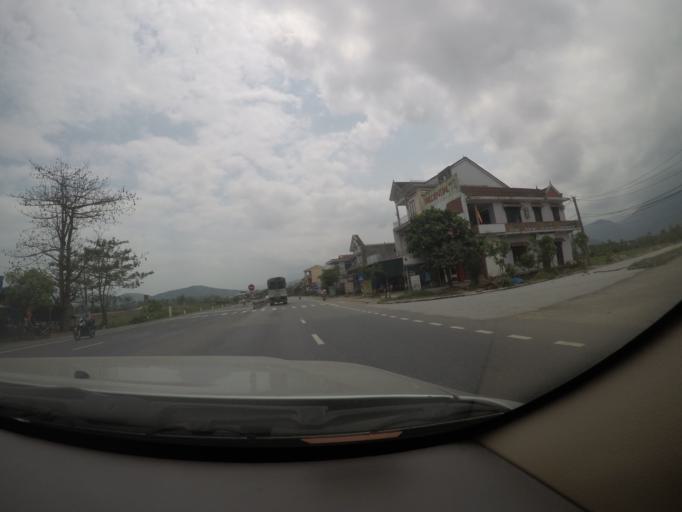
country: VN
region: Thua Thien-Hue
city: Phu Loc
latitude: 16.2728
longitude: 107.8729
